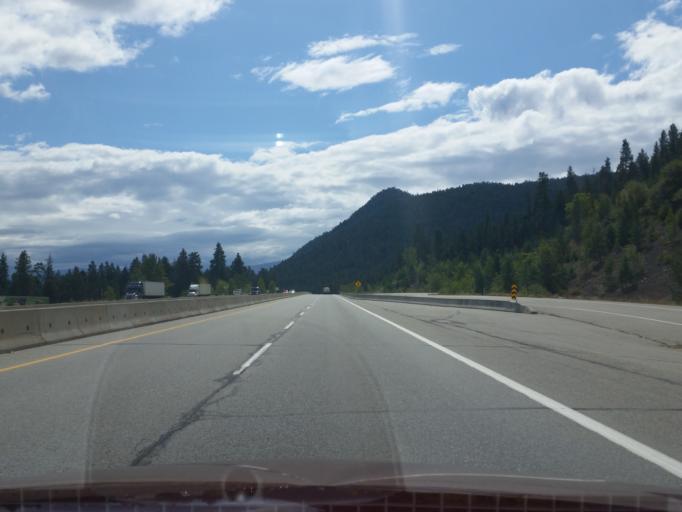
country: CA
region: British Columbia
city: Peachland
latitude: 49.8233
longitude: -119.7885
